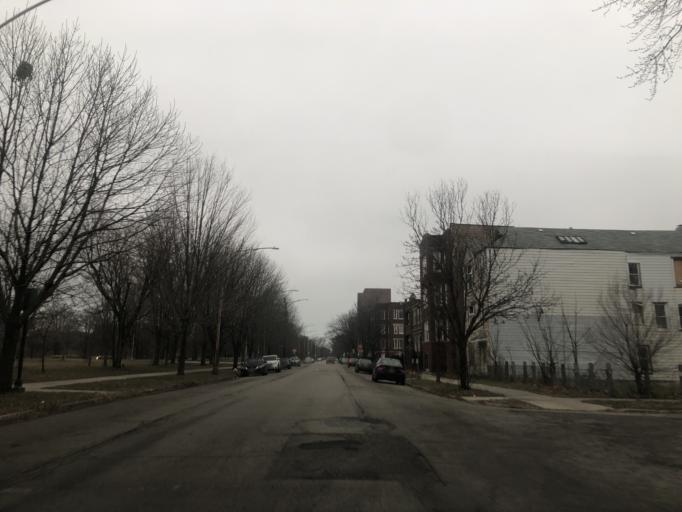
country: US
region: Illinois
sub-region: Cook County
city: Chicago
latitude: 41.7857
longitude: -87.6124
